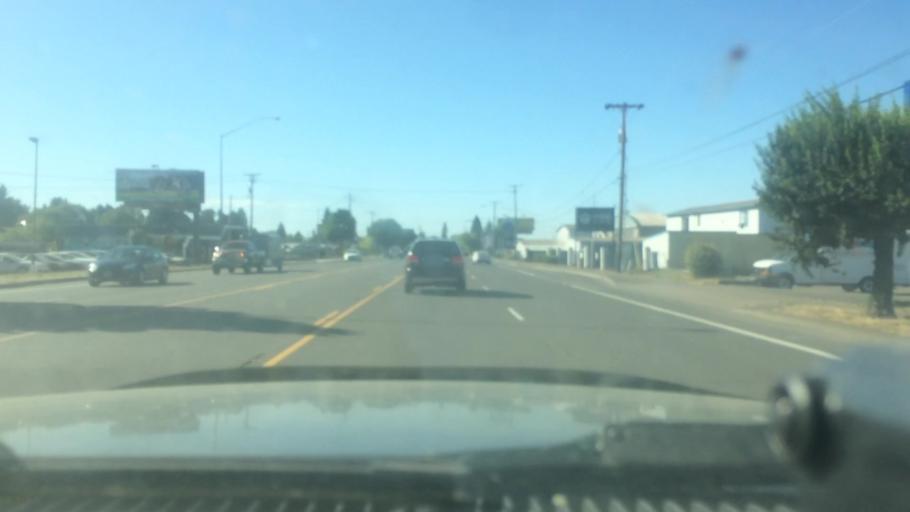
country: US
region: Oregon
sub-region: Lane County
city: Eugene
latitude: 44.0777
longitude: -123.1496
